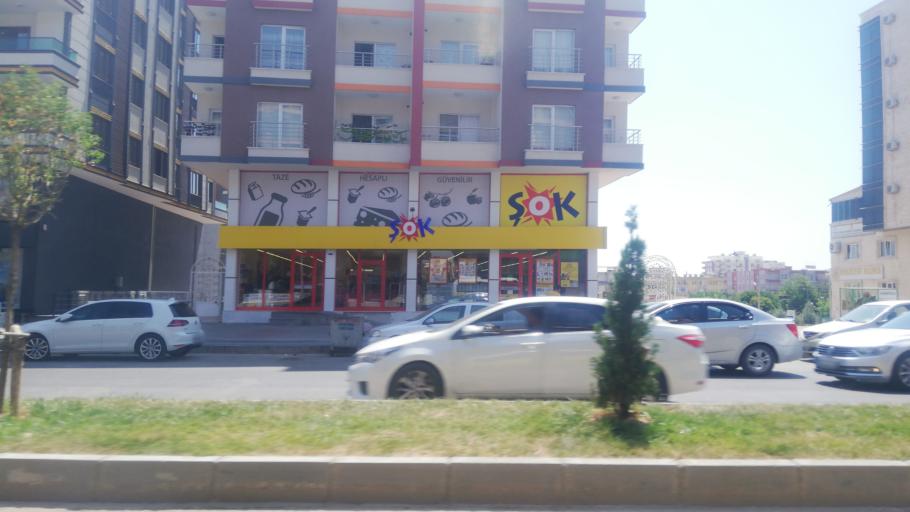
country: TR
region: Mardin
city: Midyat
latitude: 37.4193
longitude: 41.3538
